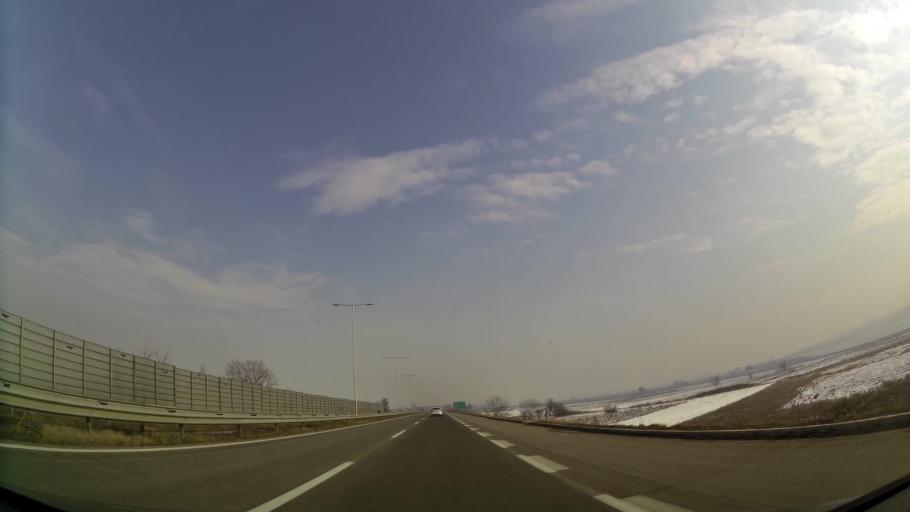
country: MK
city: Creshevo
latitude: 42.0324
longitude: 21.4882
